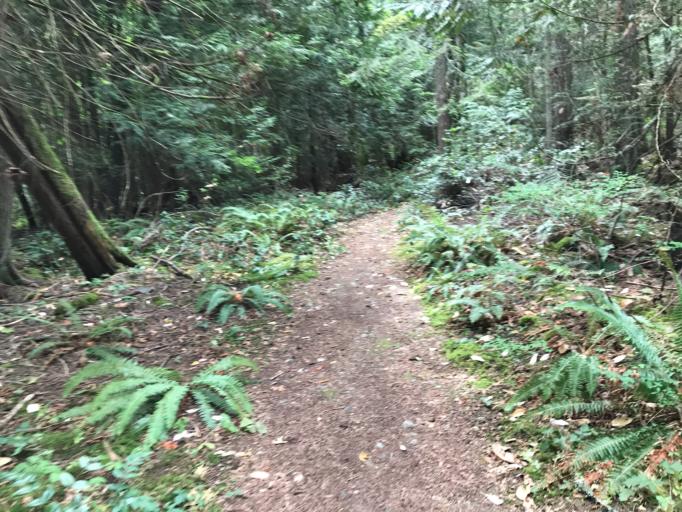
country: CA
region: British Columbia
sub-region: Cowichan Valley Regional District
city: Ladysmith
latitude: 48.9284
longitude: -123.7374
